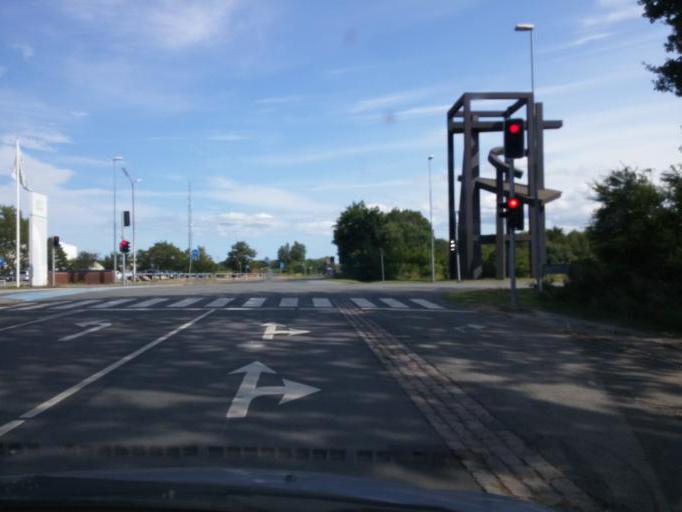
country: DK
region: South Denmark
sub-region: Kerteminde Kommune
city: Munkebo
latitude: 55.4670
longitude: 10.5381
